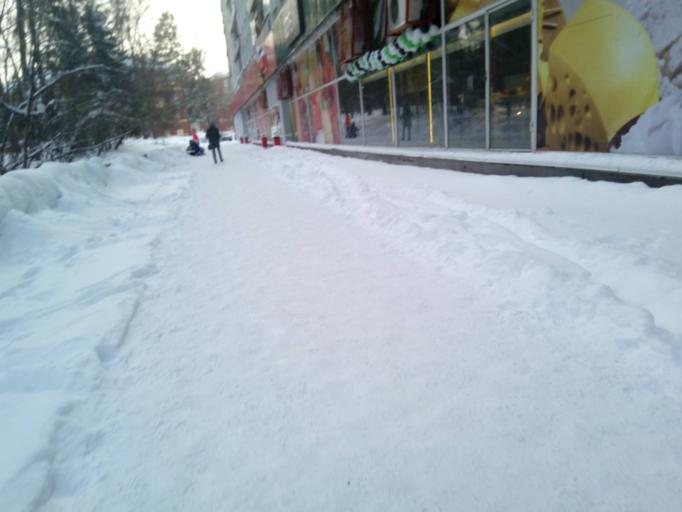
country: RU
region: Novosibirsk
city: Akademgorodok
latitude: 54.8411
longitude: 83.1022
